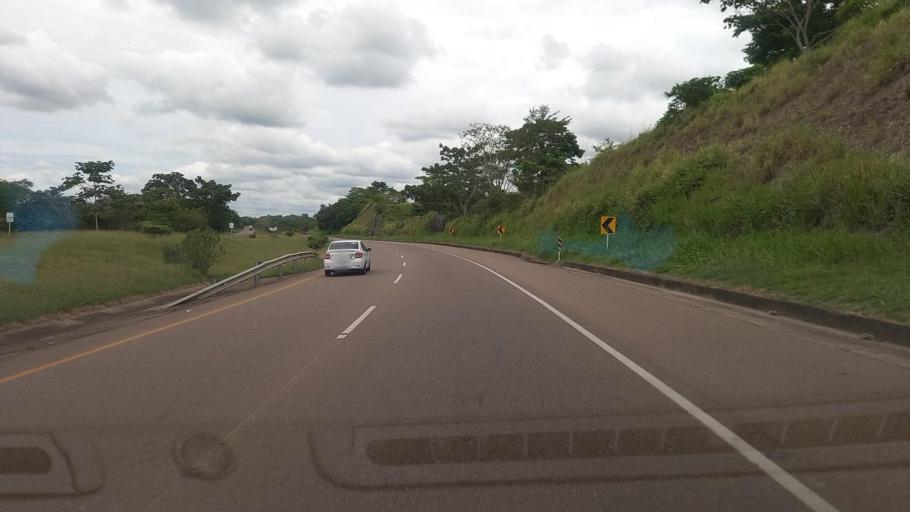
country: CO
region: Antioquia
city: Puerto Triunfo
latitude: 5.8936
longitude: -74.5684
